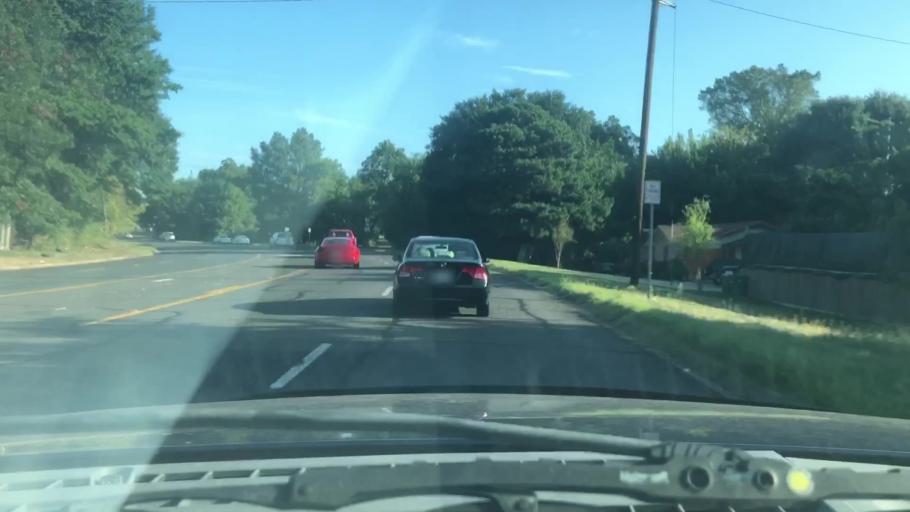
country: US
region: Texas
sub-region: Bowie County
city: Texarkana
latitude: 33.4369
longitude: -94.0627
